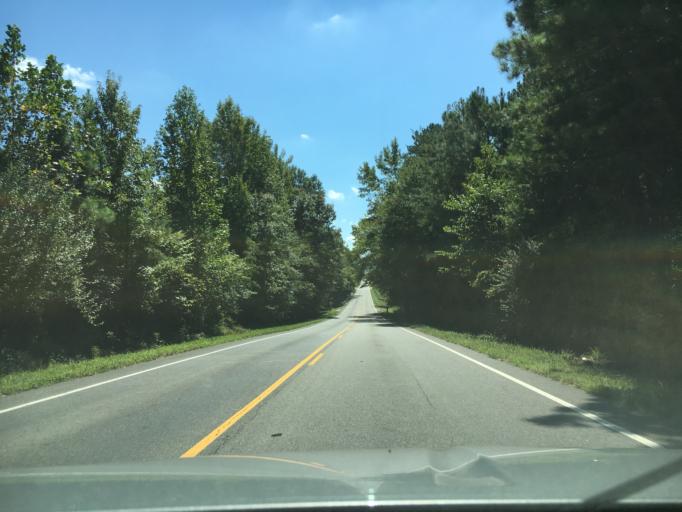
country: US
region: Virginia
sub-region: Amelia County
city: Amelia Court House
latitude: 37.4064
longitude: -77.8940
